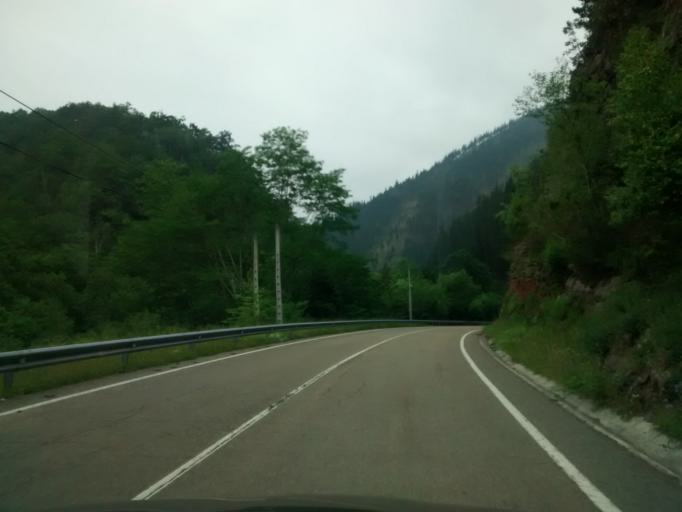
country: ES
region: Cantabria
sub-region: Provincia de Cantabria
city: Ruente
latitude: 43.1583
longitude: -4.2404
